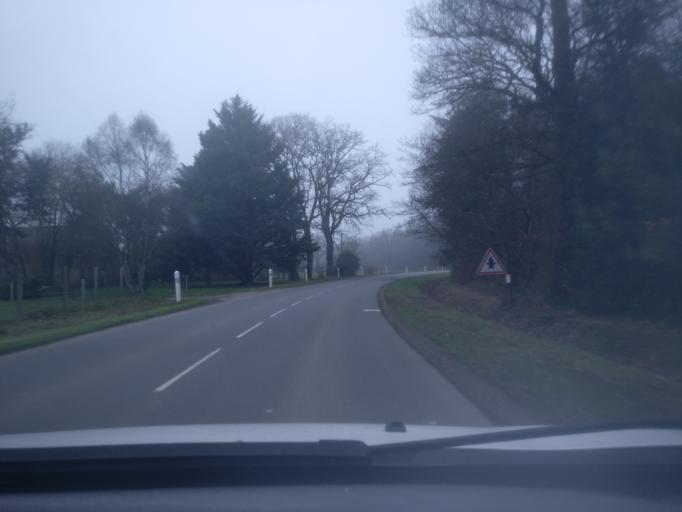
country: FR
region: Brittany
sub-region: Departement d'Ille-et-Vilaine
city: Saint-Medard-sur-Ille
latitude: 48.2796
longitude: -1.6142
